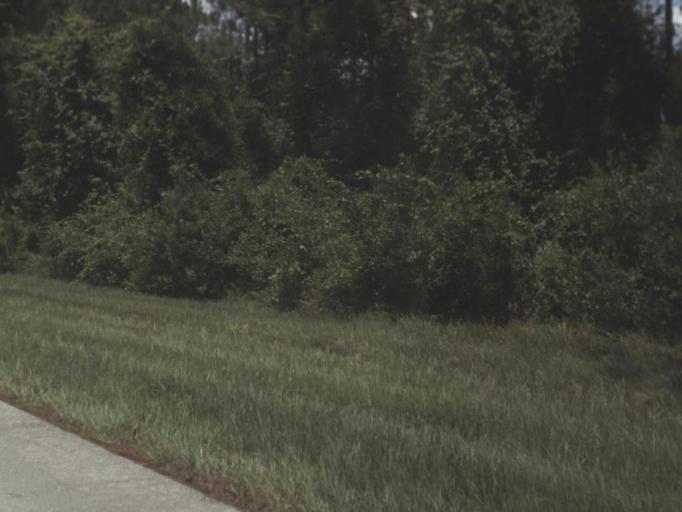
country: US
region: Florida
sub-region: Baker County
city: Macclenny
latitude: 30.1587
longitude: -82.1848
